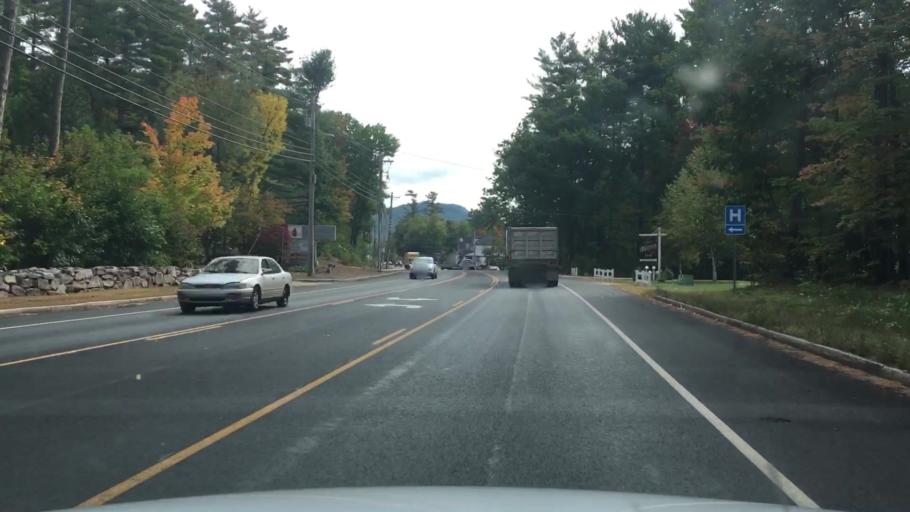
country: US
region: New Hampshire
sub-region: Carroll County
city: North Conway
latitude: 44.0604
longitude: -71.1384
